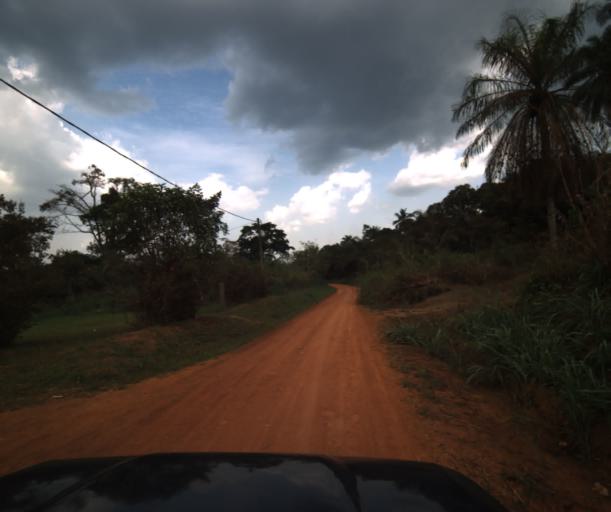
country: CM
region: Centre
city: Akono
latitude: 3.5972
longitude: 11.1740
